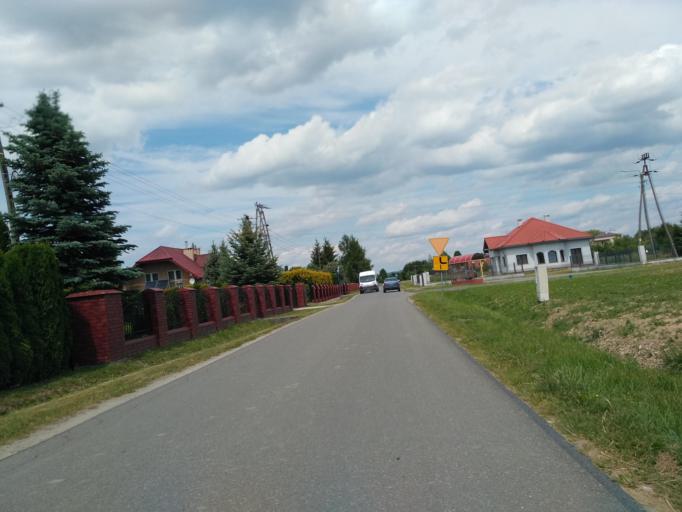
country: PL
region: Subcarpathian Voivodeship
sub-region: Powiat krosnienski
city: Chorkowka
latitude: 49.6858
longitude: 21.7024
